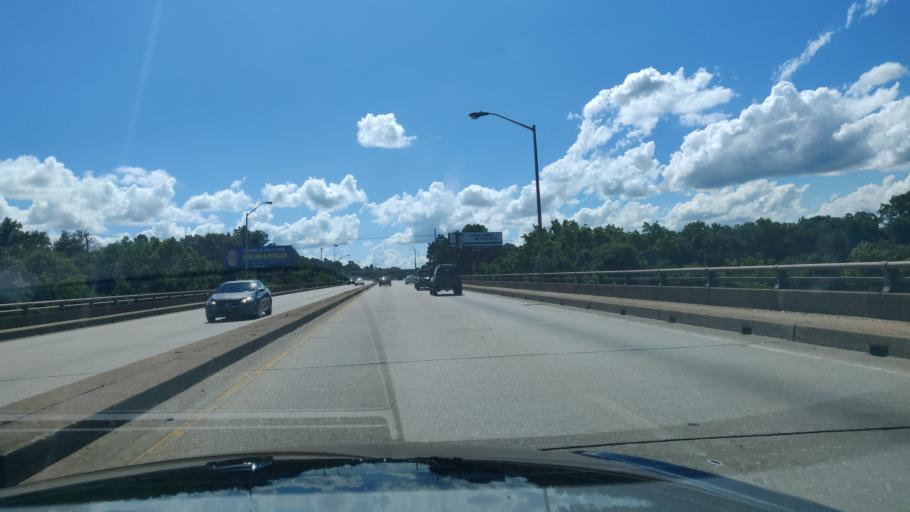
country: US
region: Georgia
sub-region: Muscogee County
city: Columbus
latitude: 32.4531
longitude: -84.9949
